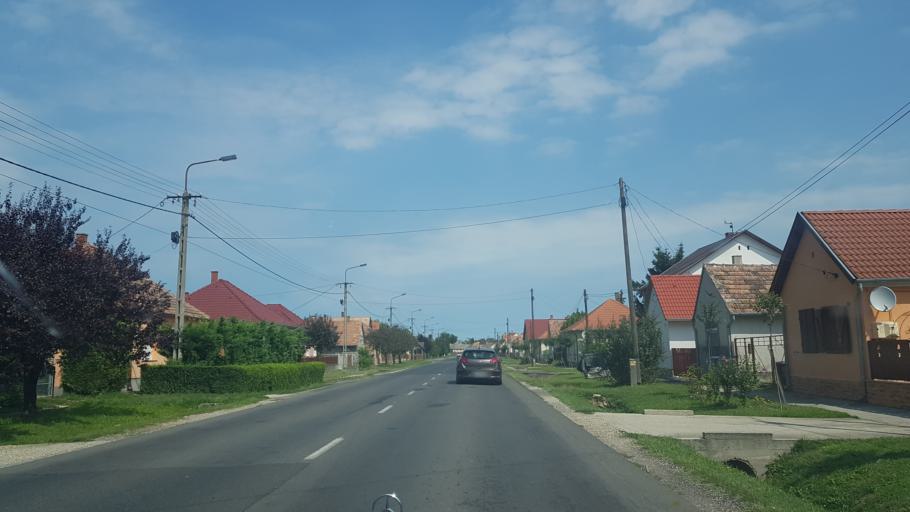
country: HU
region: Somogy
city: Kethely
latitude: 46.6360
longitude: 17.3958
